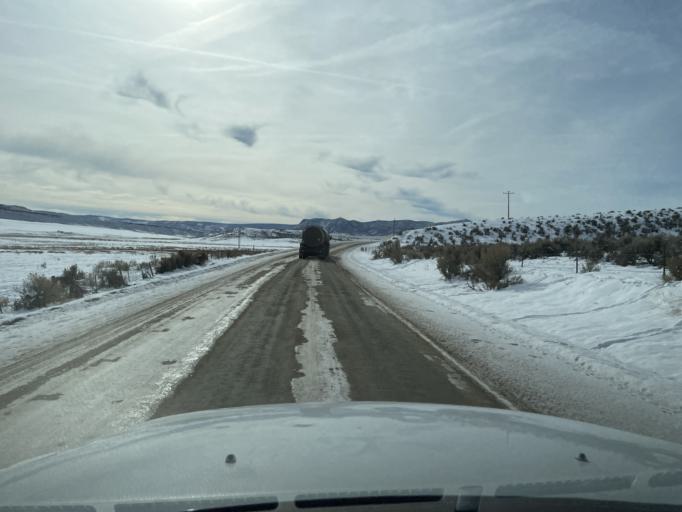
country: US
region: Colorado
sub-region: Moffat County
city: Craig
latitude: 40.3254
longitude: -107.6870
